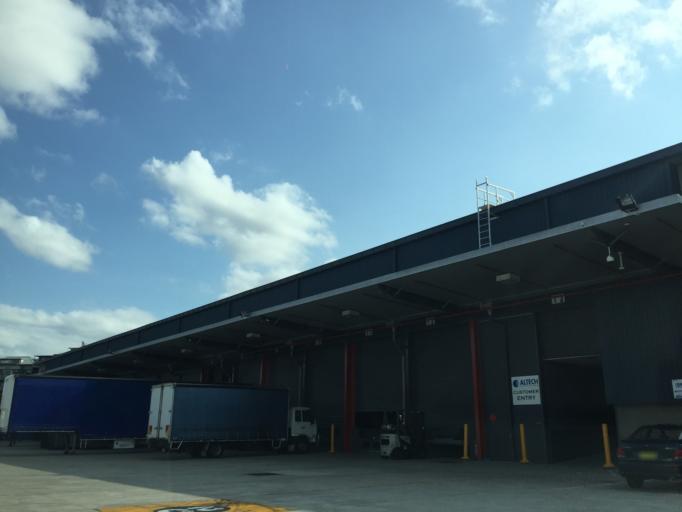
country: AU
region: New South Wales
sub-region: Strathfield
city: Homebush
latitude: -33.8599
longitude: 151.0638
